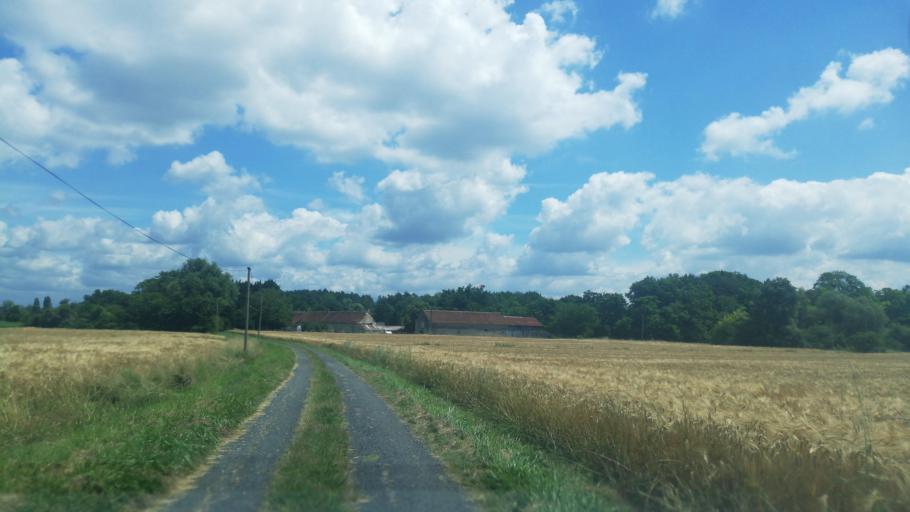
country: FR
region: Centre
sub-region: Departement du Loir-et-Cher
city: Saint-Romain-sur-Cher
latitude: 47.3431
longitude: 1.4209
